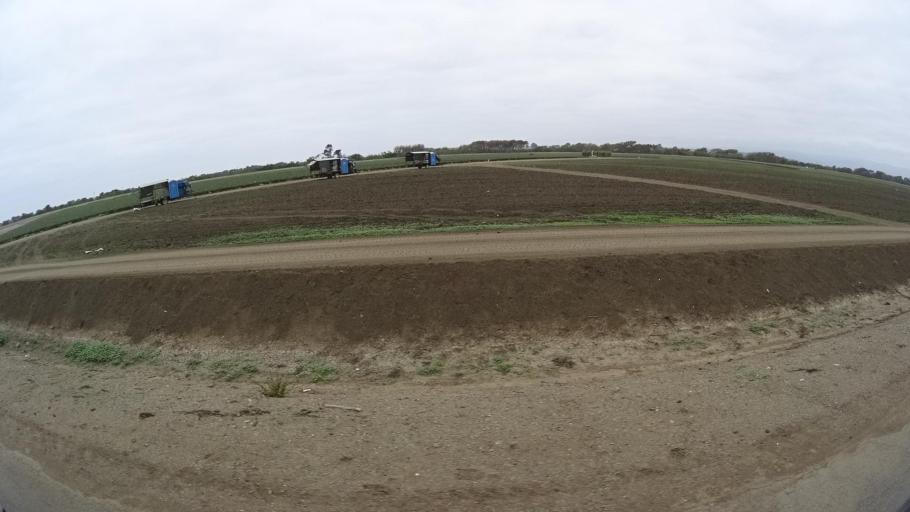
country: US
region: California
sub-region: Santa Cruz County
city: Watsonville
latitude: 36.8645
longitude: -121.7967
